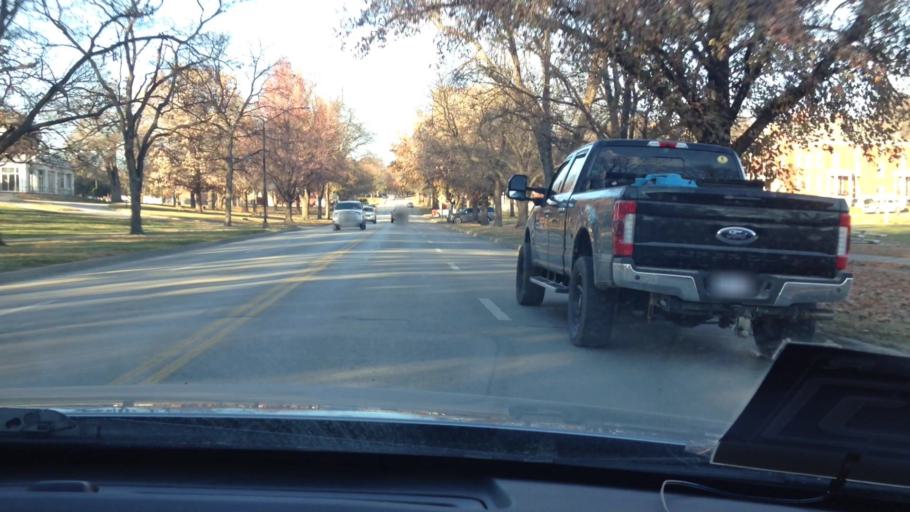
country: US
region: Kansas
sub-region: Leavenworth County
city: Leavenworth
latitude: 39.3491
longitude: -94.9190
